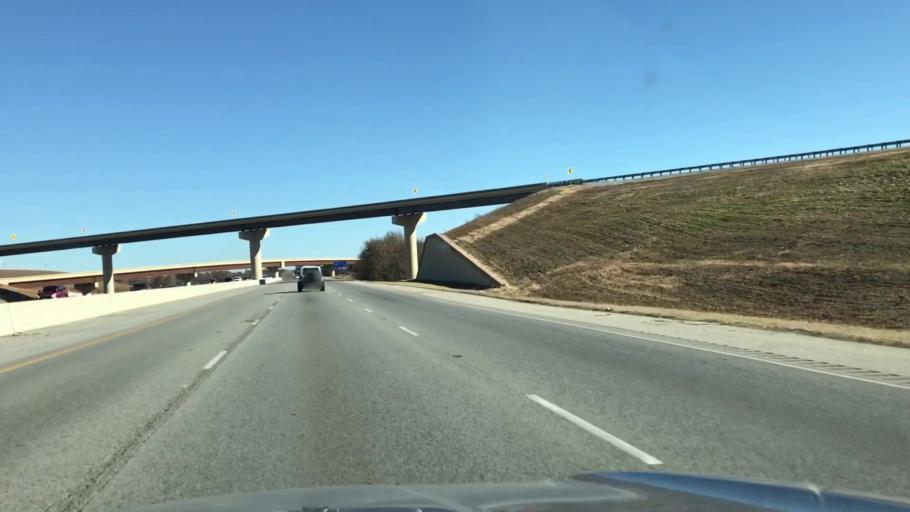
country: US
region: Arkansas
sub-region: Benton County
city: Lowell
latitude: 36.2366
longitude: -94.1626
